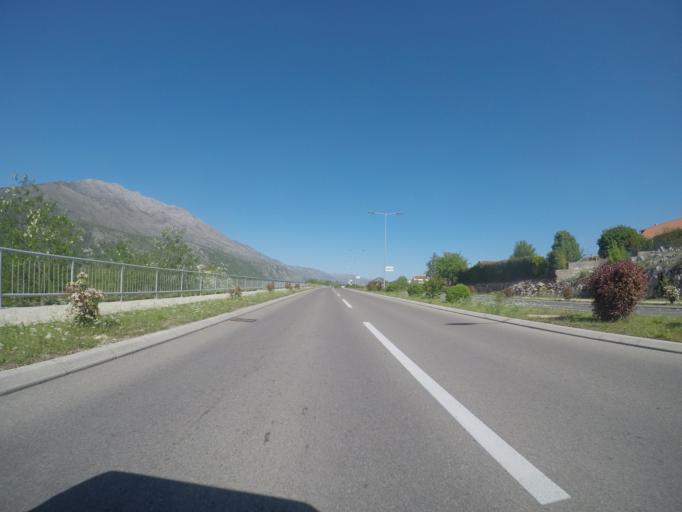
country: ME
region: Danilovgrad
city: Danilovgrad
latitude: 42.5490
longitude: 19.0953
